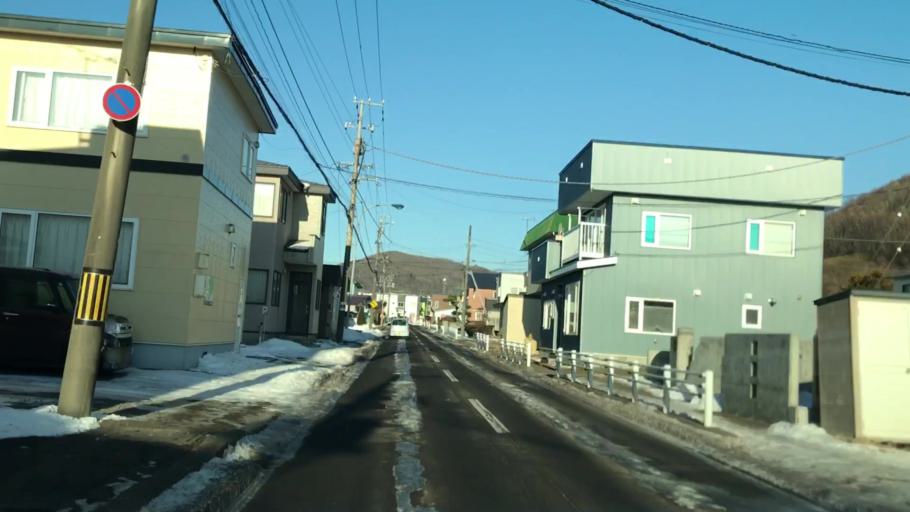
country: JP
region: Hokkaido
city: Muroran
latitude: 42.3647
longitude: 141.0433
